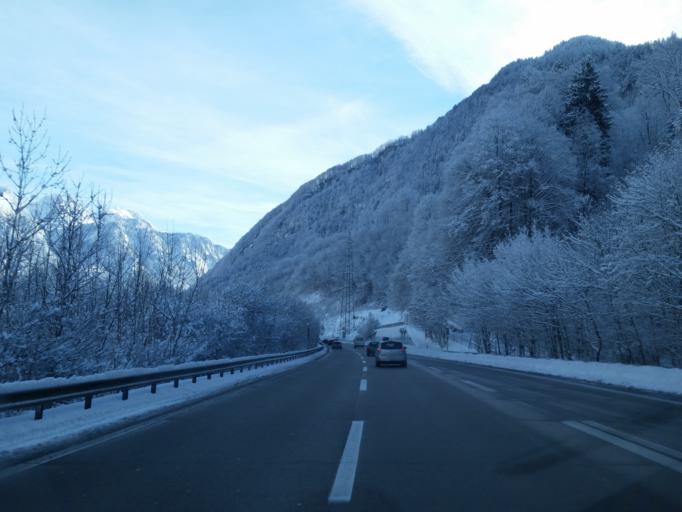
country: CH
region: Saint Gallen
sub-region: Wahlkreis Sarganserland
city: Quarten
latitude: 47.1112
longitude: 9.2720
